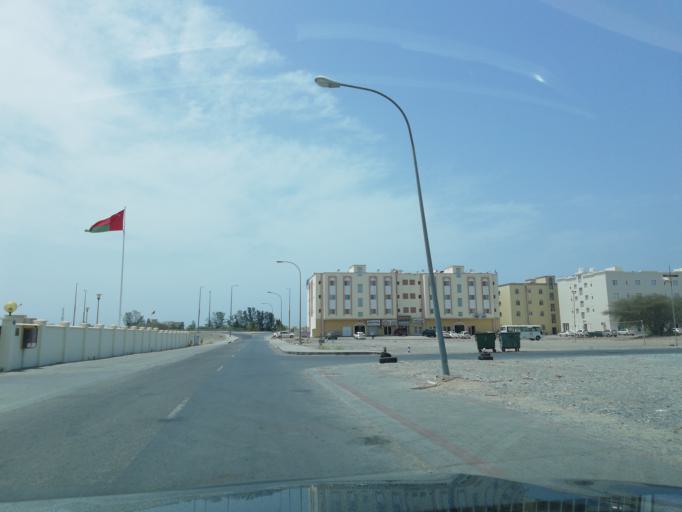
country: OM
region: Muhafazat Masqat
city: As Sib al Jadidah
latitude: 23.6629
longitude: 58.1934
